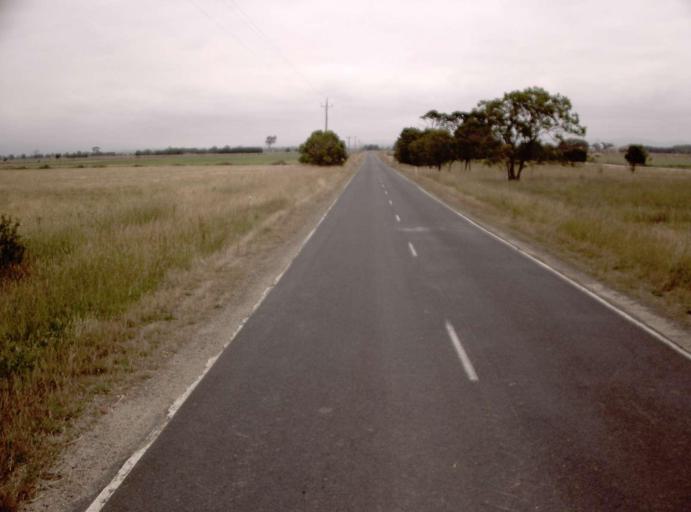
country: AU
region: Victoria
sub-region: Wellington
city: Heyfield
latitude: -38.0371
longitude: 146.7667
